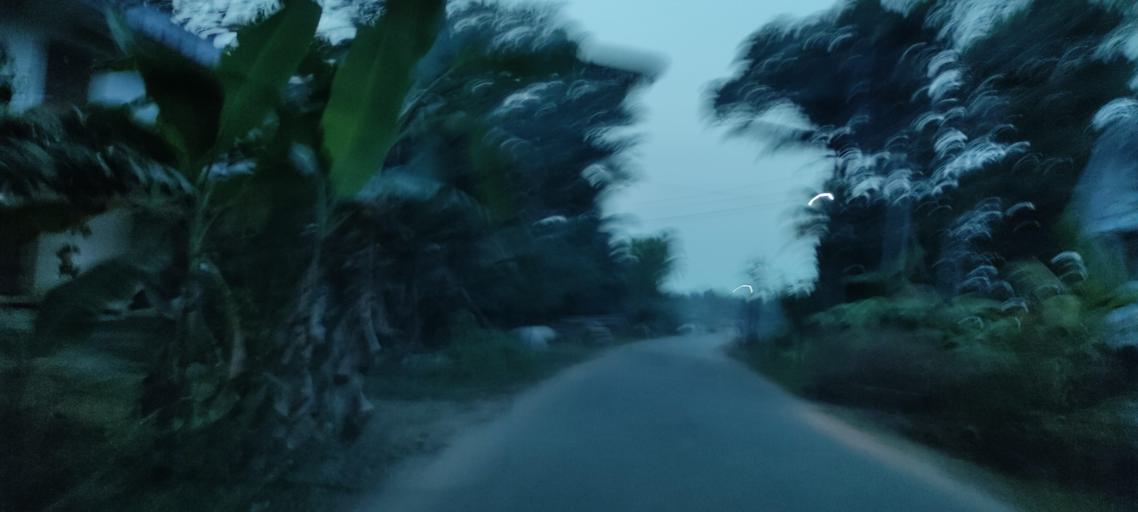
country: IN
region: Kerala
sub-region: Alappuzha
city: Mavelikara
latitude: 9.3297
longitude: 76.4703
